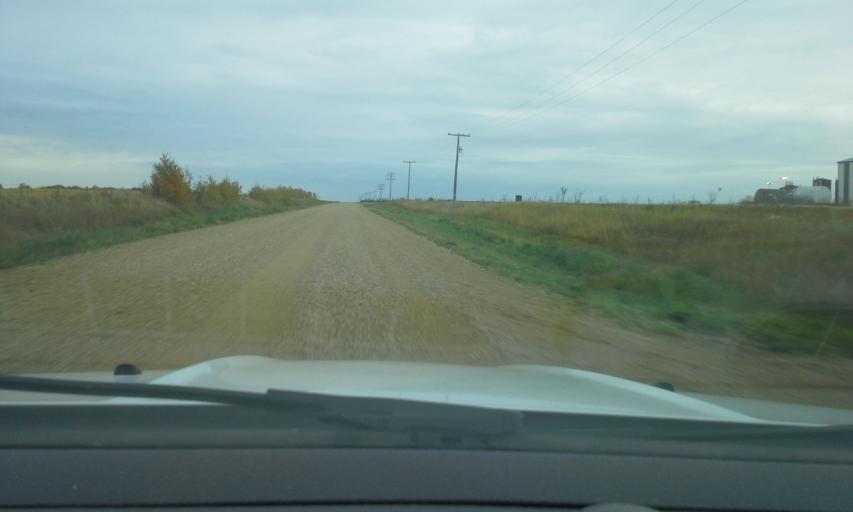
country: CA
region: Saskatchewan
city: Lloydminster
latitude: 53.2943
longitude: -109.8085
